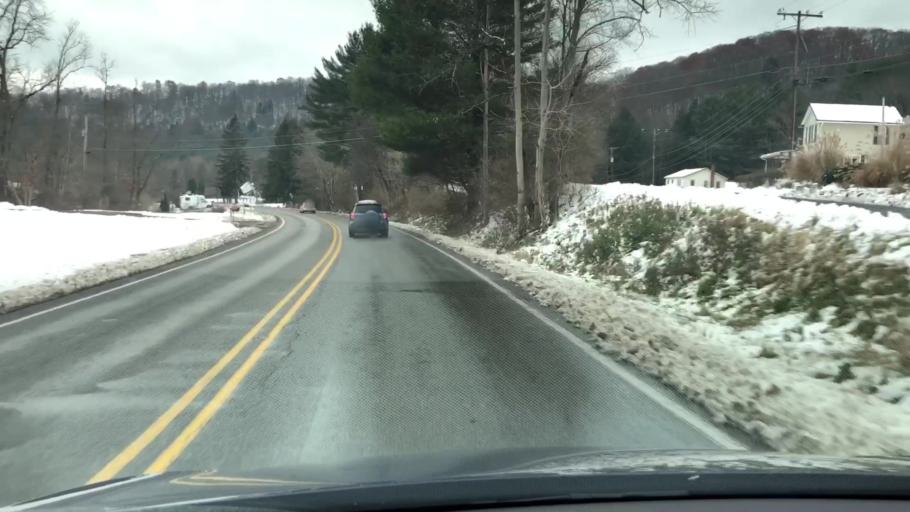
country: US
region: Pennsylvania
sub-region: Clearfield County
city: Treasure Lake
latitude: 41.2417
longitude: -78.5442
